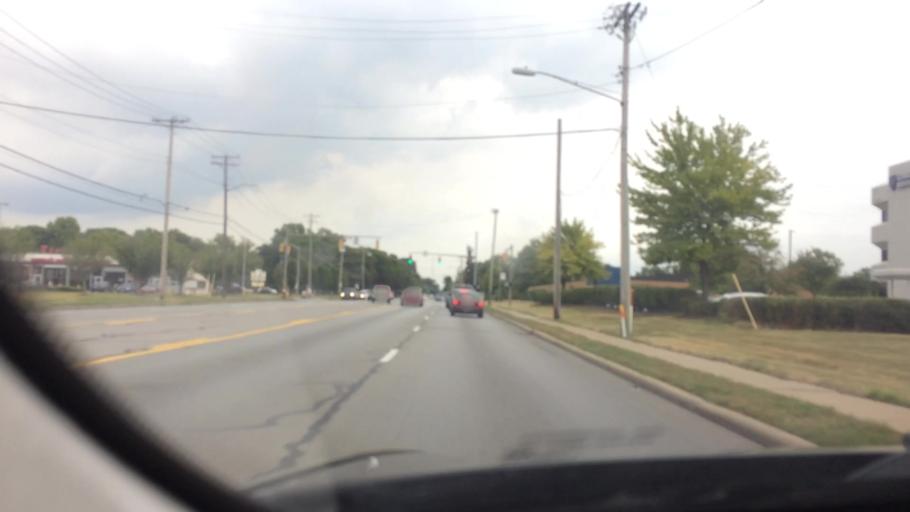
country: US
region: Ohio
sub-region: Lucas County
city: Ottawa Hills
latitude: 41.6124
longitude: -83.6236
